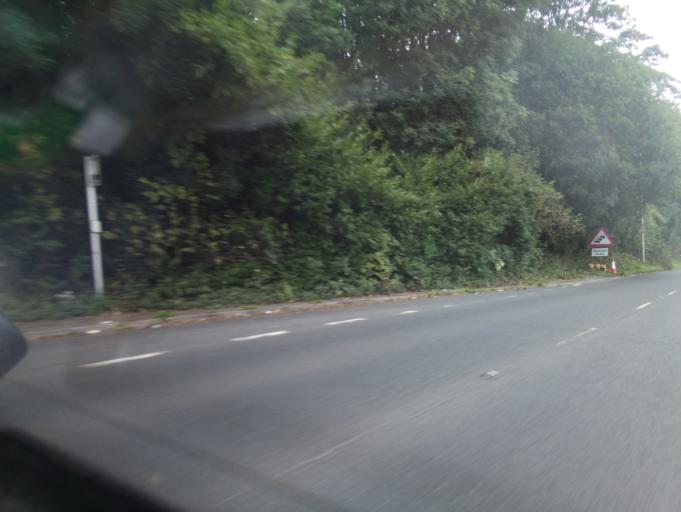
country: GB
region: England
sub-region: Devon
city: Exminster
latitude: 50.6890
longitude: -3.5042
